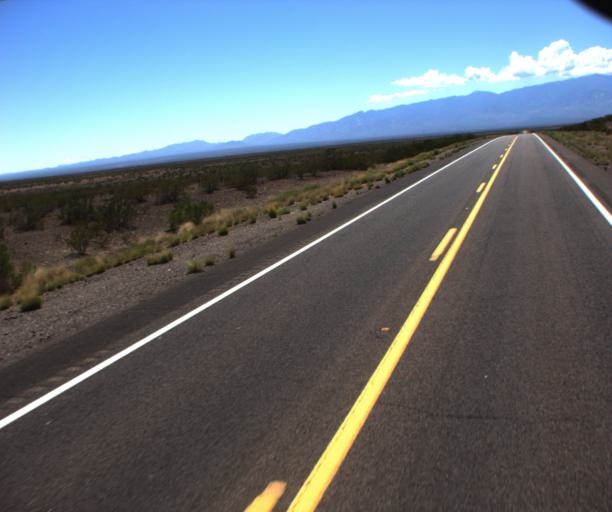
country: US
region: Arizona
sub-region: Graham County
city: Safford
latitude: 32.8036
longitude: -109.5201
